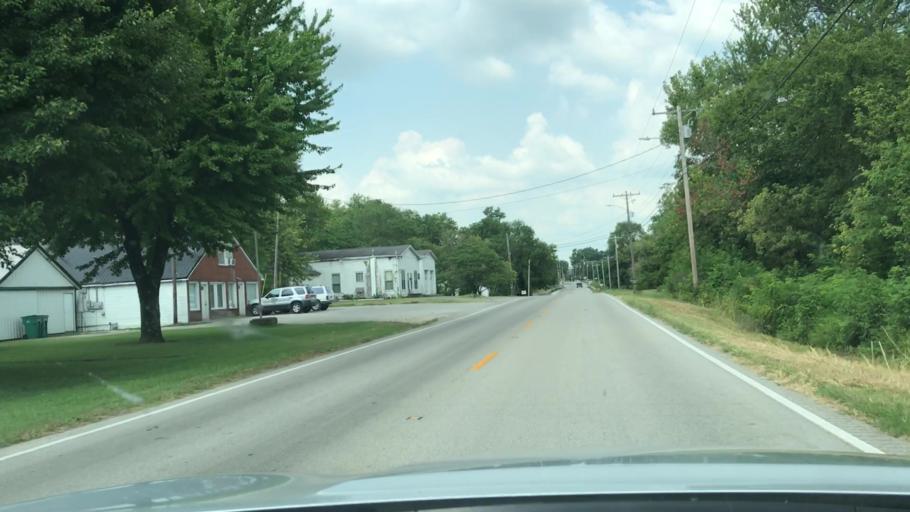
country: US
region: Kentucky
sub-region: Todd County
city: Elkton
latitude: 36.8078
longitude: -87.1426
